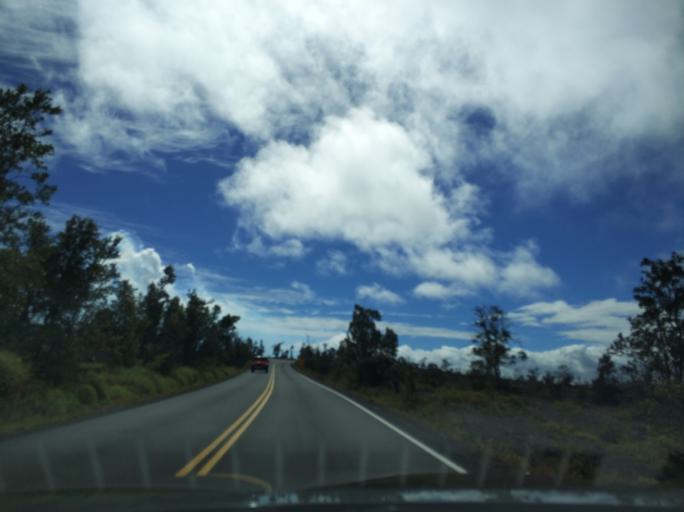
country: US
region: Hawaii
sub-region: Hawaii County
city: Volcano
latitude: 19.4222
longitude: -155.2887
